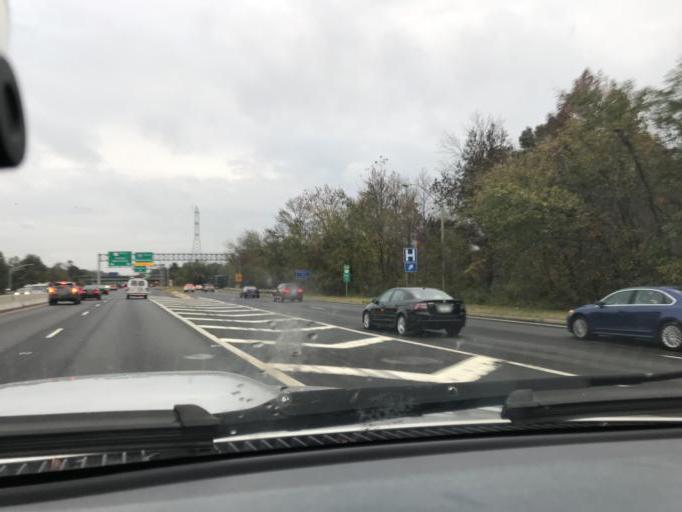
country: US
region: New Jersey
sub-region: Mercer County
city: Lawrenceville
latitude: 40.2869
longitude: -74.6920
